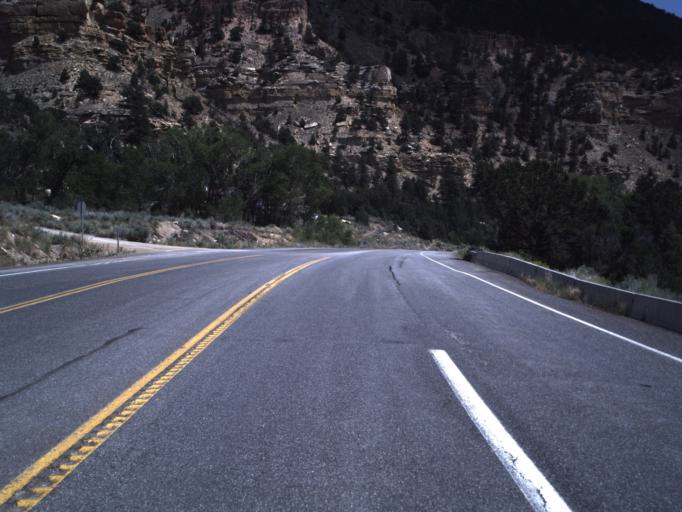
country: US
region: Utah
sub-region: Emery County
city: Huntington
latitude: 39.4155
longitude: -111.1195
